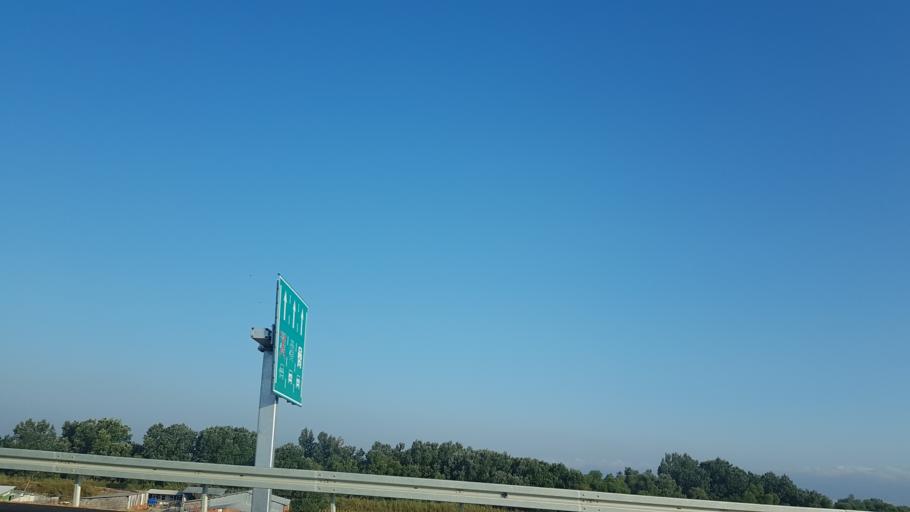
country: TR
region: Bursa
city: Karacabey
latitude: 40.1858
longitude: 28.3350
